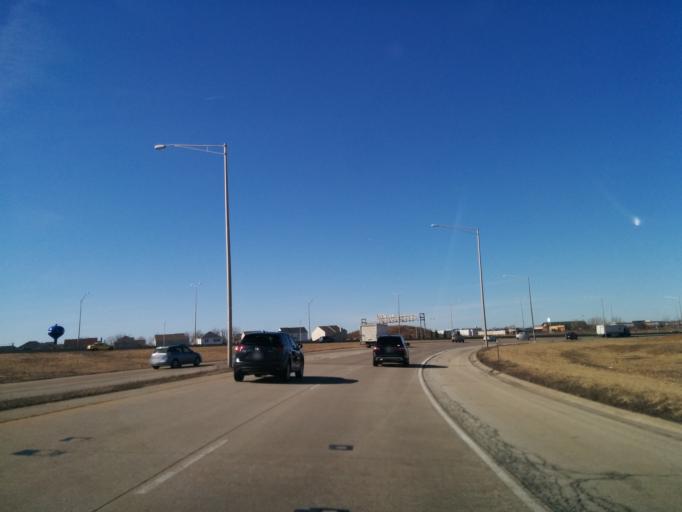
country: US
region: Illinois
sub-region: Will County
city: Bolingbrook
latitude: 41.7084
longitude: -88.0295
